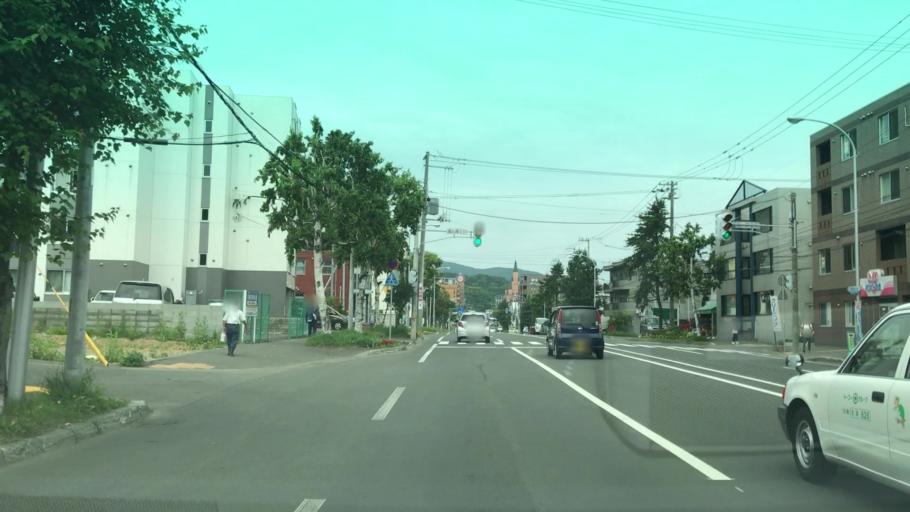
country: JP
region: Hokkaido
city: Sapporo
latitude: 43.0566
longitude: 141.3041
